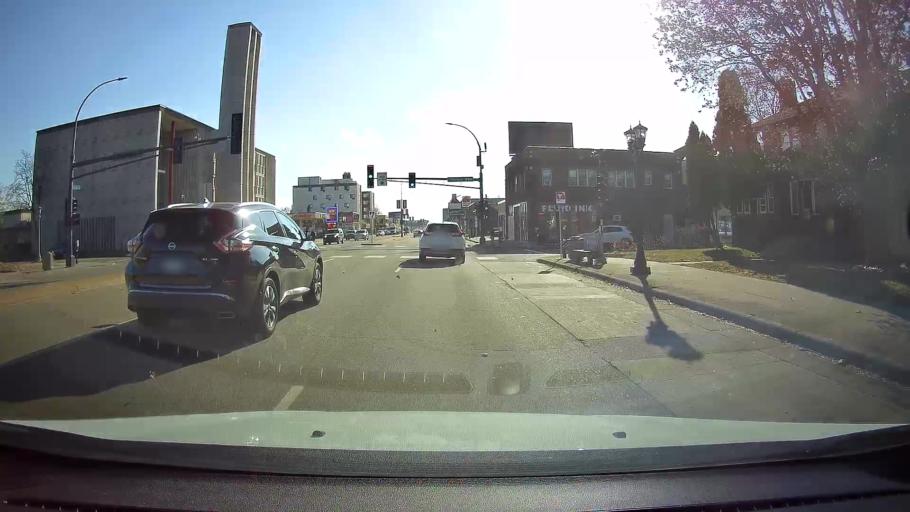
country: US
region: Minnesota
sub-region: Ramsey County
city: Falcon Heights
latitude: 44.9597
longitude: -93.1671
